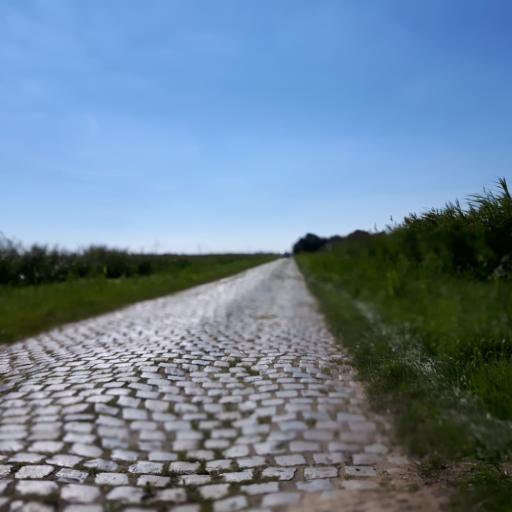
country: NL
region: North Brabant
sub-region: Gemeente Woensdrecht
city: Woensdrecht
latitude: 51.4368
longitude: 4.2742
